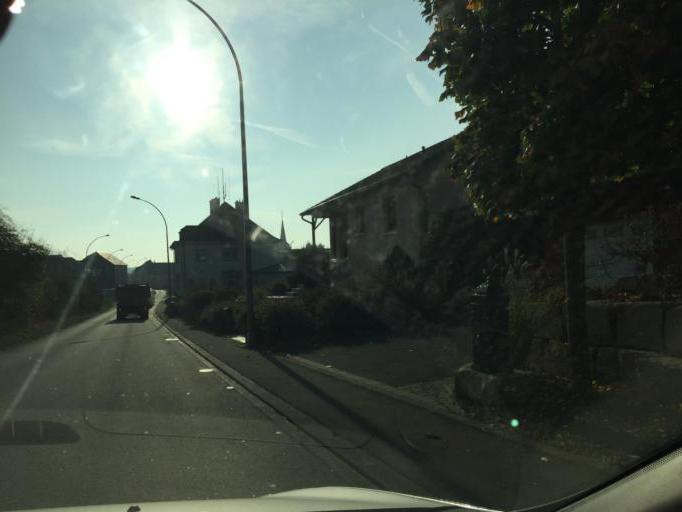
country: LU
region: Grevenmacher
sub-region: Canton de Remich
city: Dalheim
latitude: 49.5354
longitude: 6.2447
